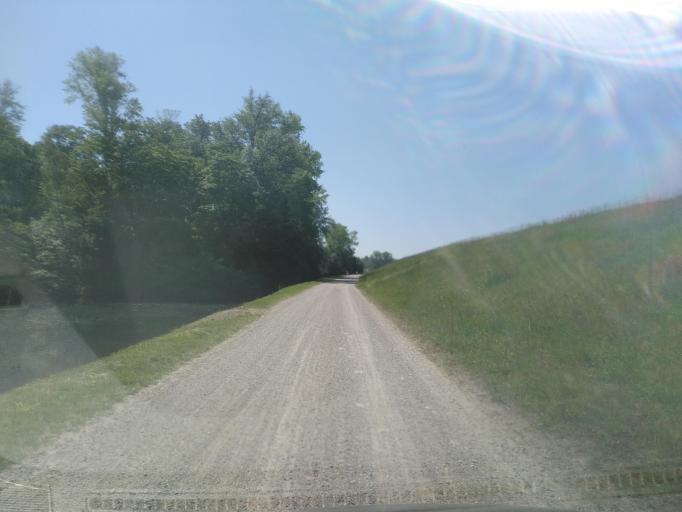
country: FR
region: Alsace
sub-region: Departement du Haut-Rhin
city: Kunheim
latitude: 48.0969
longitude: 7.5799
